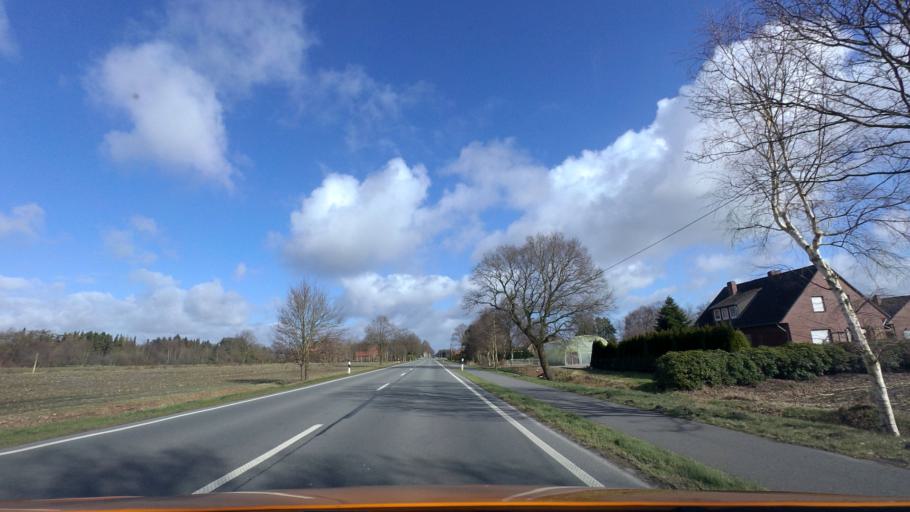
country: DE
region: Lower Saxony
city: Bosel
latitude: 53.0656
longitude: 7.9202
